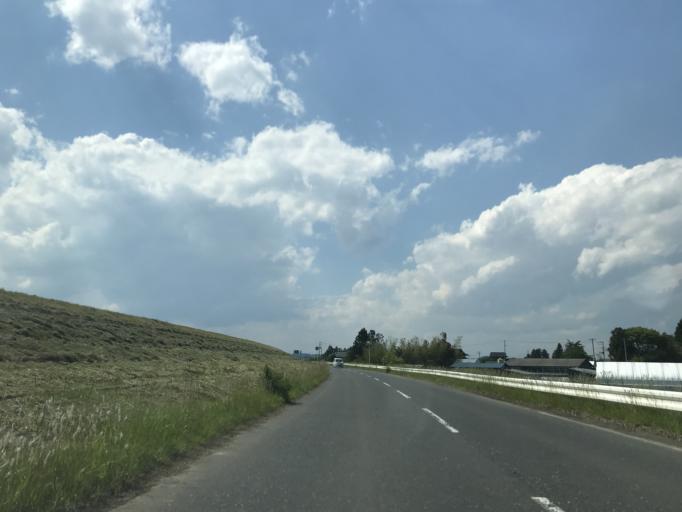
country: JP
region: Miyagi
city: Matsushima
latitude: 38.4433
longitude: 141.1147
